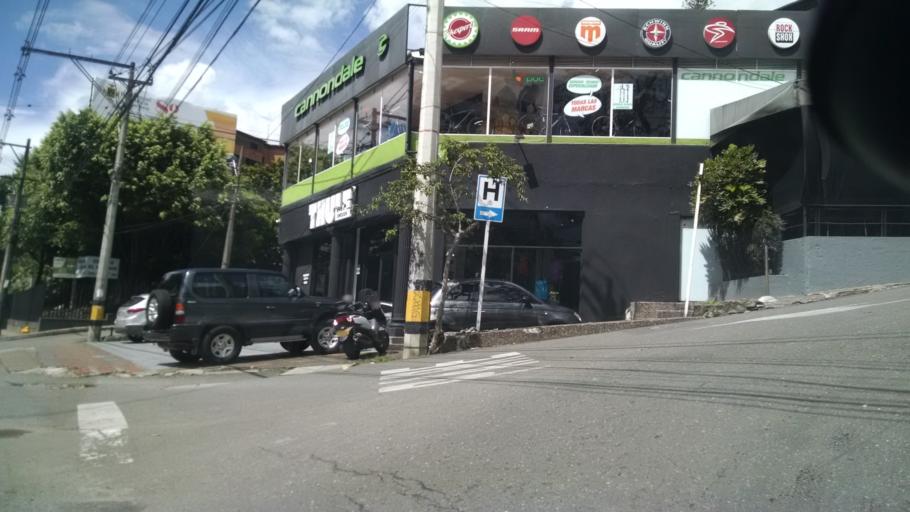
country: CO
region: Antioquia
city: Medellin
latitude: 6.2128
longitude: -75.5699
